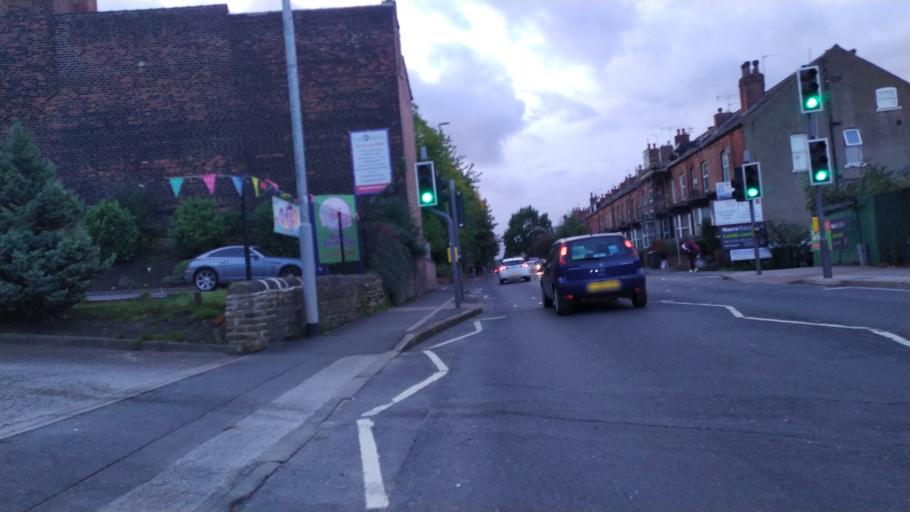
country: GB
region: England
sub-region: City and Borough of Leeds
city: Chapel Allerton
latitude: 53.8171
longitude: -1.5488
